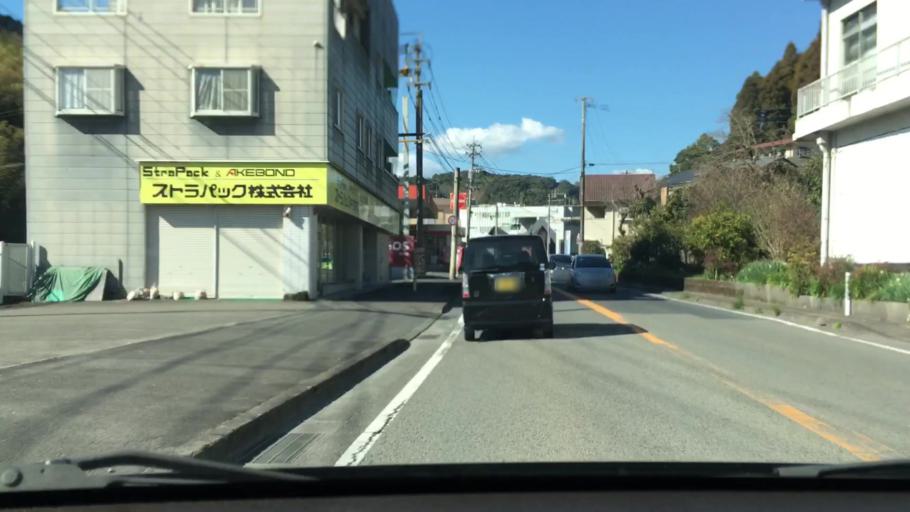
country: JP
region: Kagoshima
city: Kagoshima-shi
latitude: 31.6395
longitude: 130.5177
